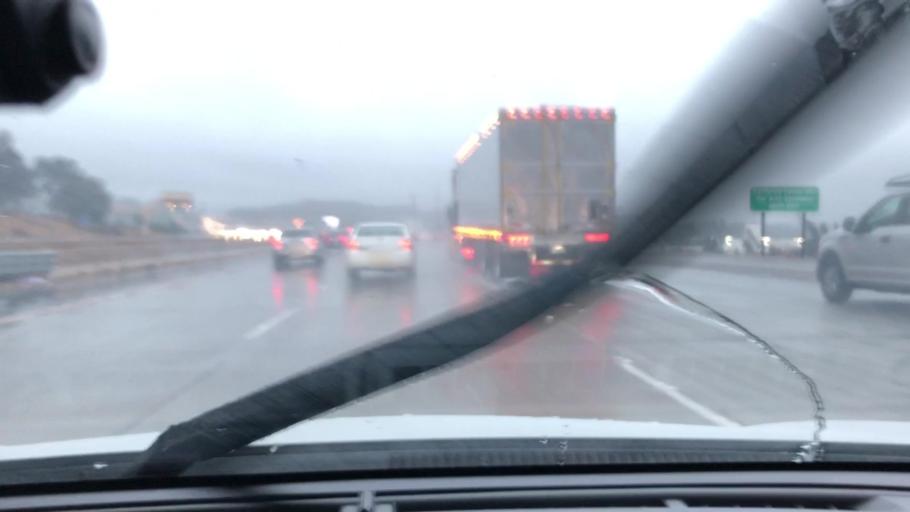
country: US
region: California
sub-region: San Diego County
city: Escondido
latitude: 33.1265
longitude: -117.1049
